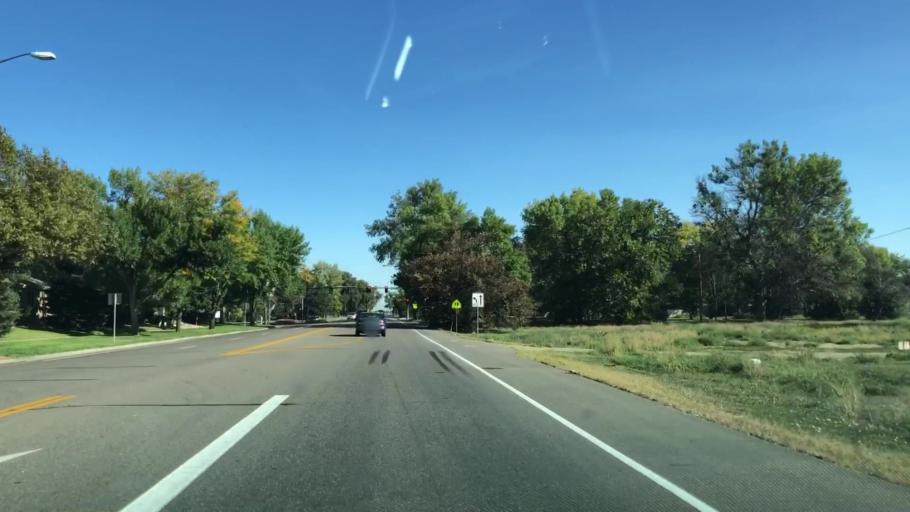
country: US
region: Colorado
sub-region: Larimer County
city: Loveland
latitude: 40.4205
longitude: -105.0586
